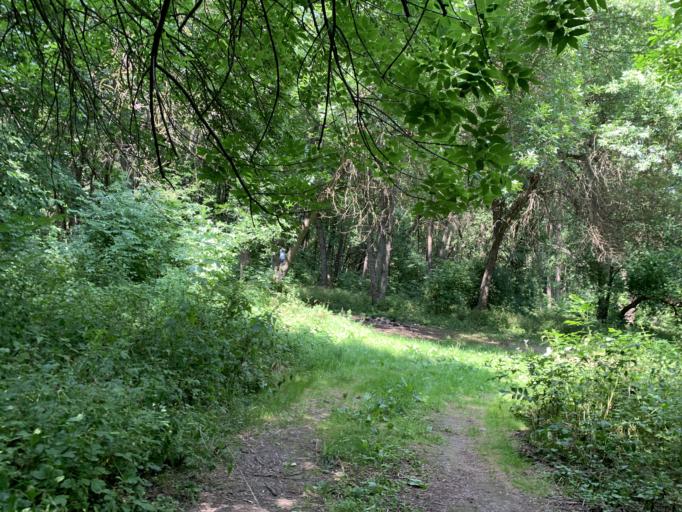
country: BY
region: Minsk
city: Nyasvizh
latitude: 53.2320
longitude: 26.7045
